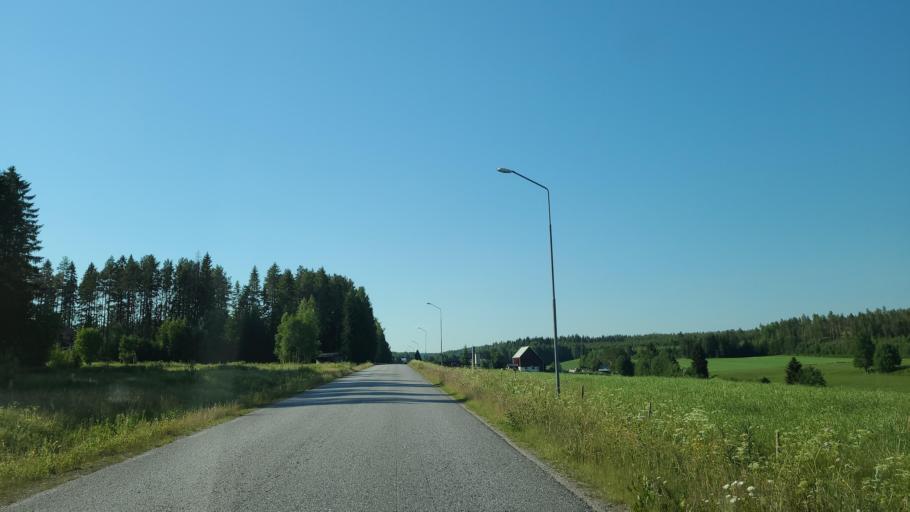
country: SE
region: Vaesterbotten
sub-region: Robertsfors Kommun
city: Robertsfors
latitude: 64.2733
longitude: 20.8098
